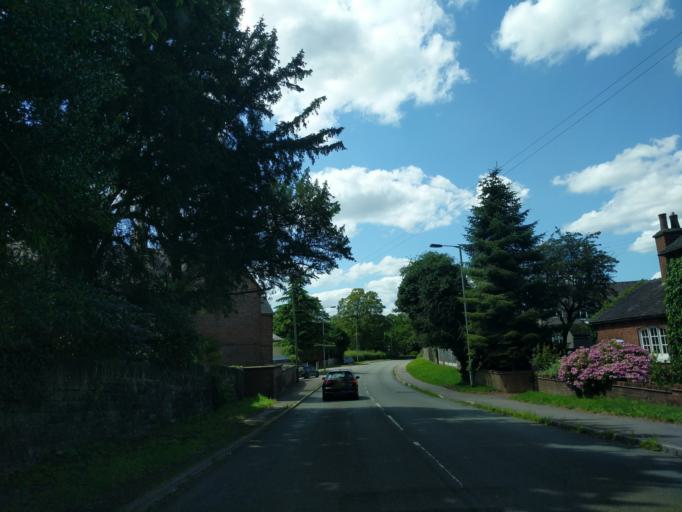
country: GB
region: England
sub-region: Staffordshire
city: Cheadle
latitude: 52.9437
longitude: -1.9725
